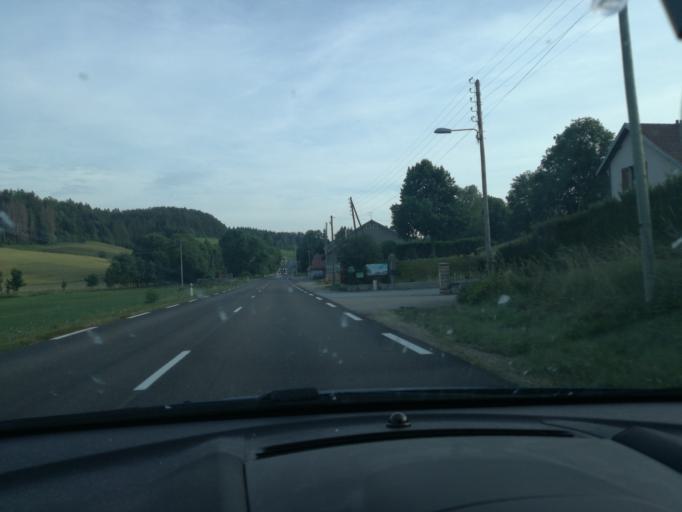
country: FR
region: Franche-Comte
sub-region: Departement du Jura
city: Morbier
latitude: 46.6017
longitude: 5.9614
